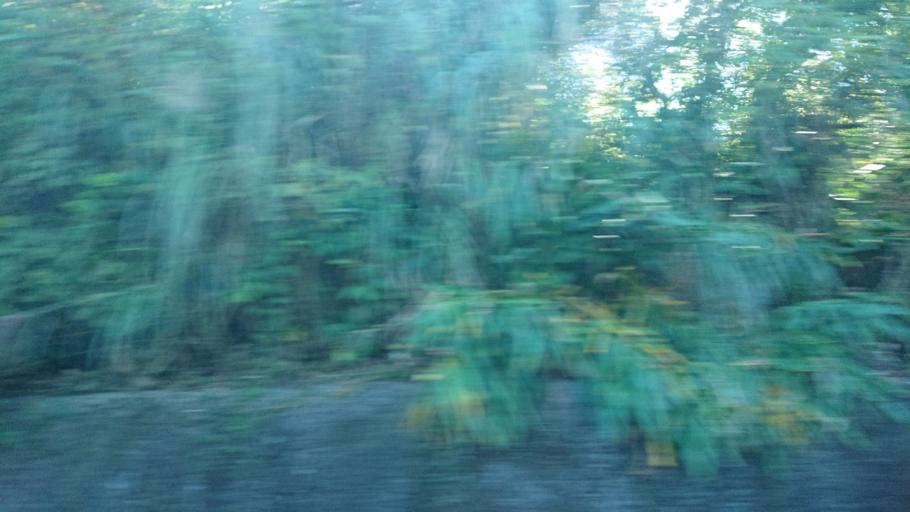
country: TW
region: Taiwan
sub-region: Chiayi
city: Jiayi Shi
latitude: 23.5221
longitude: 120.6316
